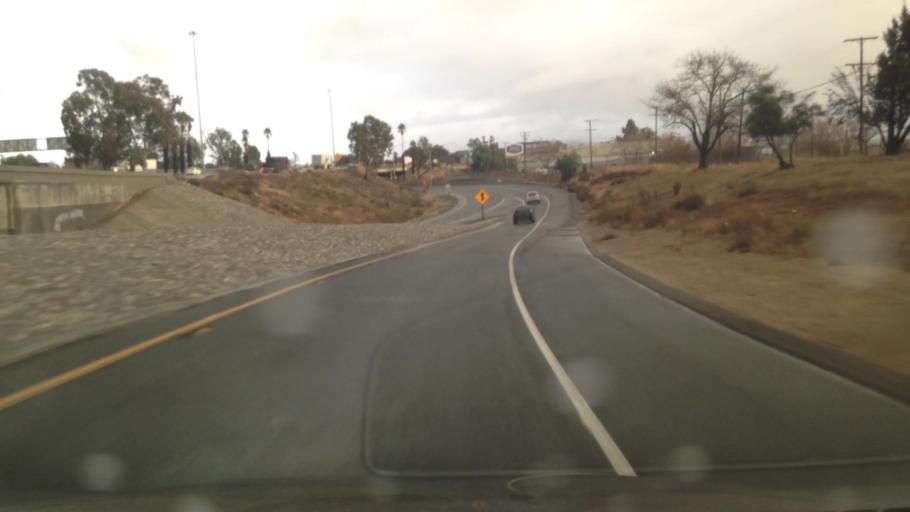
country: US
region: California
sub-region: Riverside County
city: Beaumont
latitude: 33.9326
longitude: -116.9907
